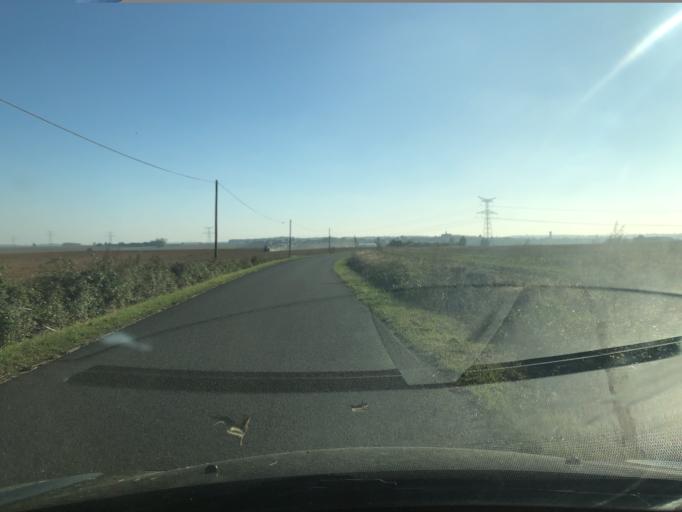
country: FR
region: Centre
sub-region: Departement d'Indre-et-Loire
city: Neuvy-le-Roi
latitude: 47.6186
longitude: 0.5993
